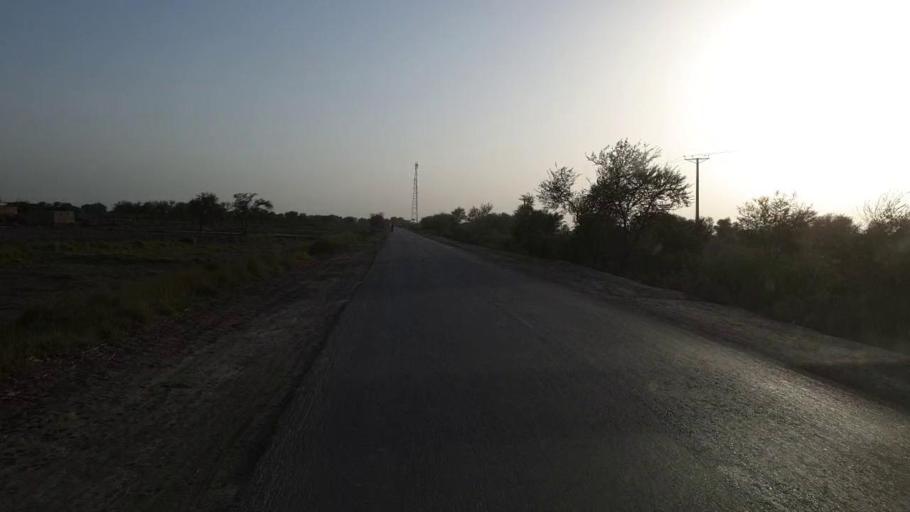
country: PK
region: Sindh
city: Jam Sahib
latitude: 26.2709
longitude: 68.5337
